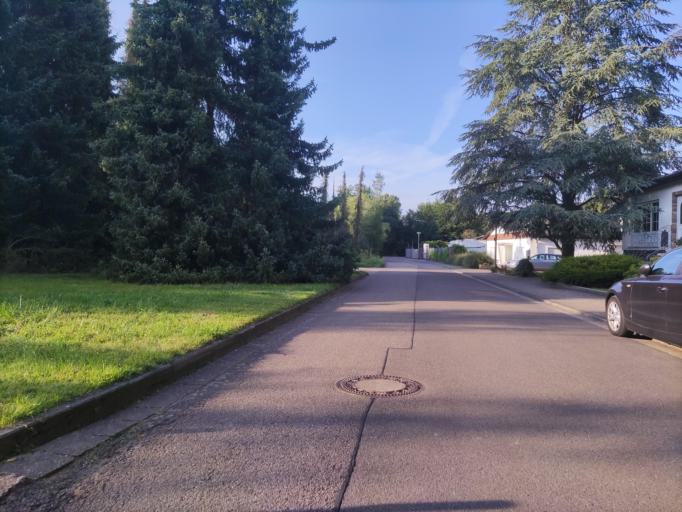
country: DE
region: Saarland
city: Wadgassen
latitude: 49.2597
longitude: 6.8000
